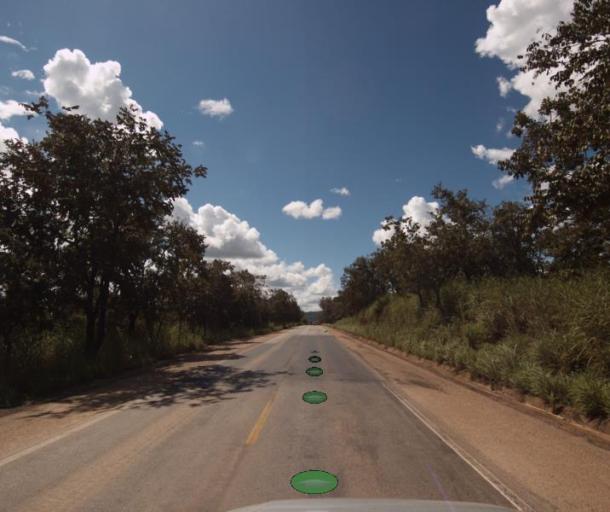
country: BR
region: Goias
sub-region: Porangatu
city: Porangatu
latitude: -13.6862
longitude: -49.0230
